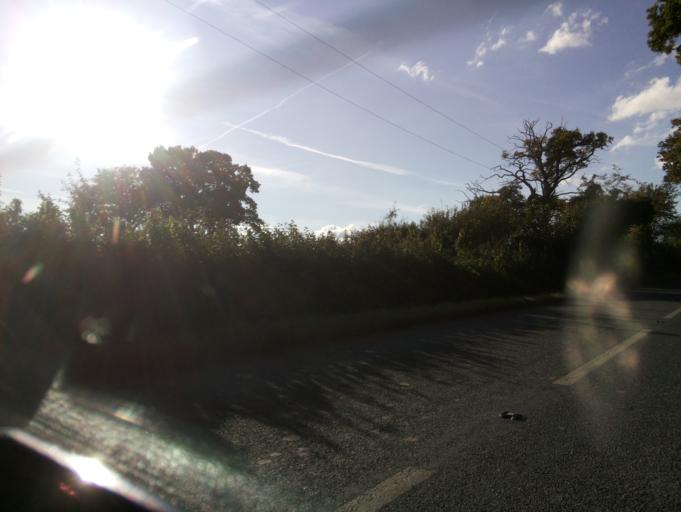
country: GB
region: England
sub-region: Herefordshire
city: Moccas
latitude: 52.0984
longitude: -2.9279
